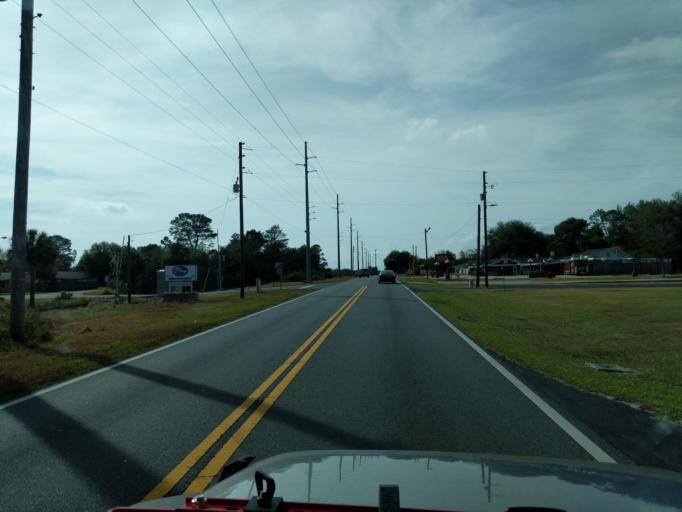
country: US
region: Florida
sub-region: Lake County
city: Mount Dora
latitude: 28.8060
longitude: -81.6805
